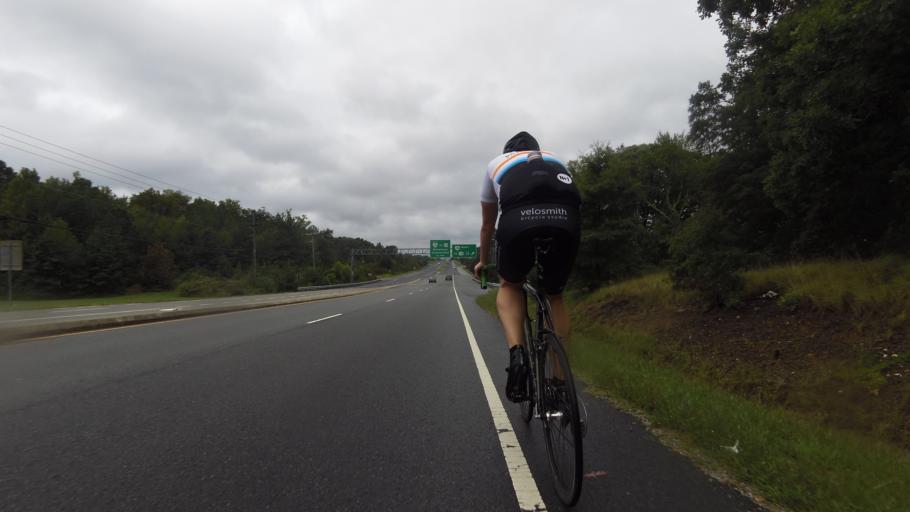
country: US
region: Virginia
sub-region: Henrico County
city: Short Pump
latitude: 37.5995
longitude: -77.6555
